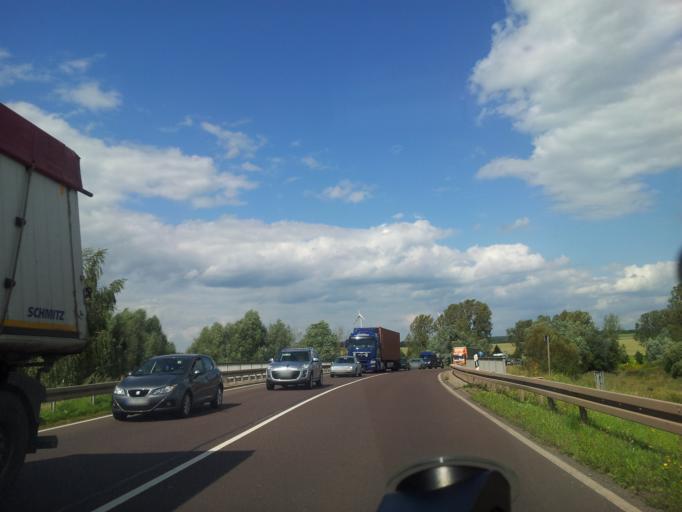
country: DE
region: Saxony-Anhalt
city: Haldensleben I
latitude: 52.2848
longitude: 11.4338
